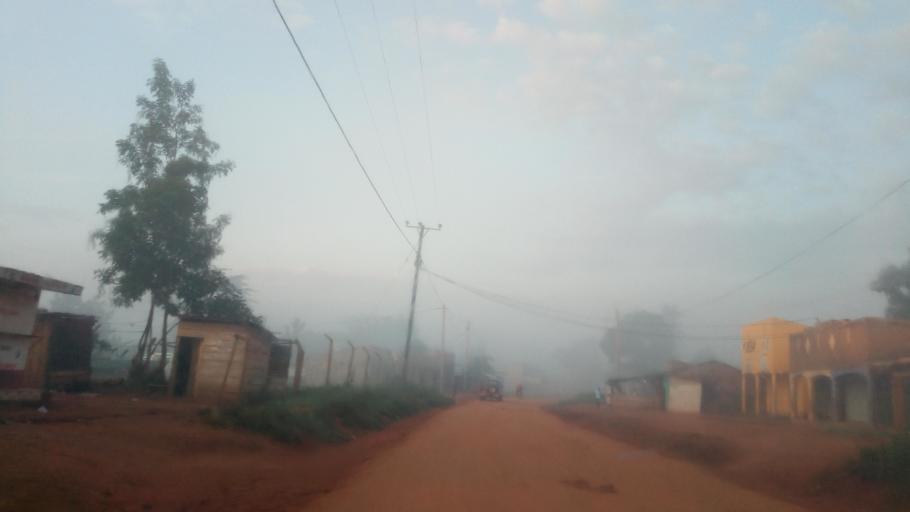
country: UG
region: Central Region
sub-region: Wakiso District
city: Bweyogerere
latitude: 0.4379
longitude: 32.6553
